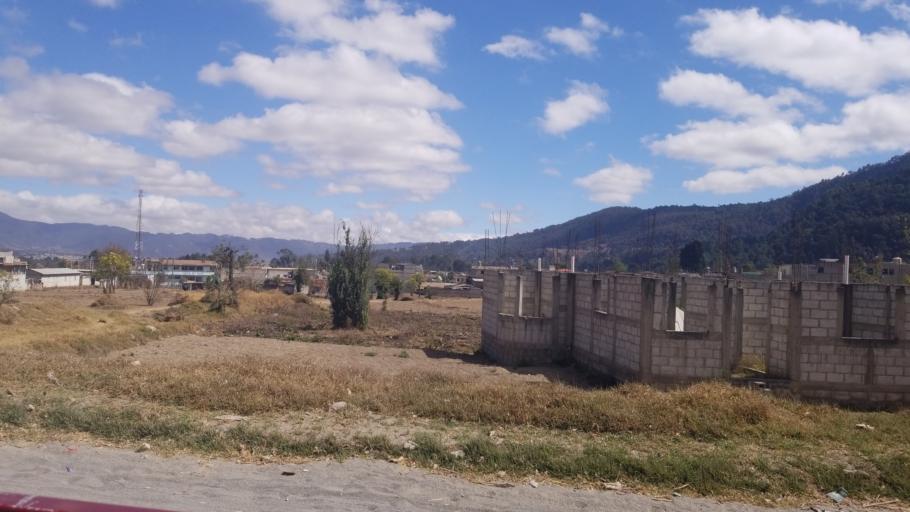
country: GT
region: Quetzaltenango
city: Almolonga
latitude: 14.7900
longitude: -91.5427
